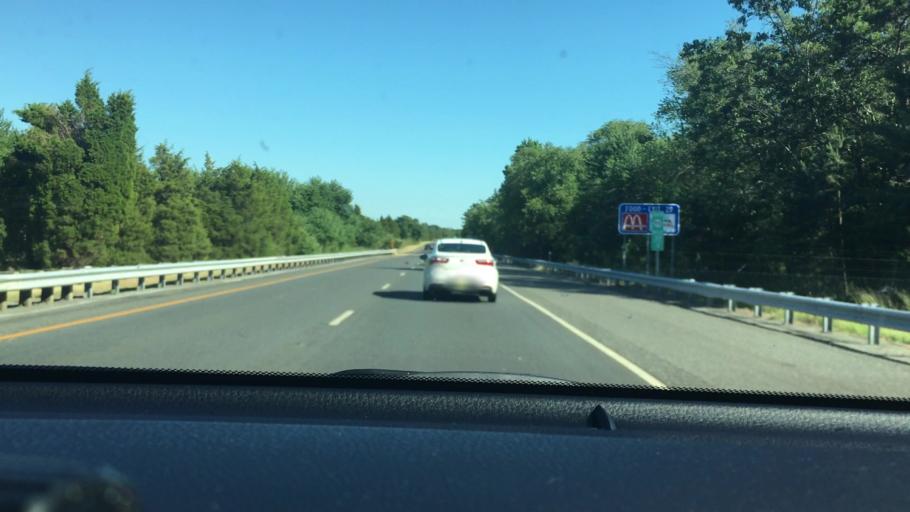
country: US
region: New Jersey
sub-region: Cumberland County
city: South Vineland
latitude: 39.4560
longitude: -75.0695
